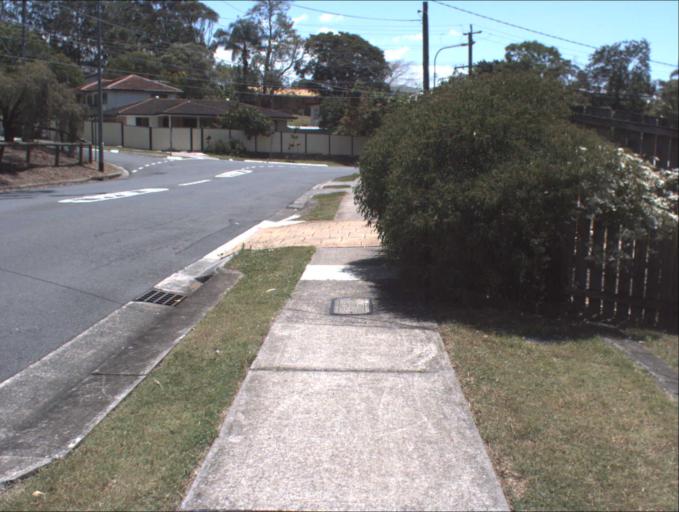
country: AU
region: Queensland
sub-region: Logan
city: Rochedale South
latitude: -27.5983
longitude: 153.1330
